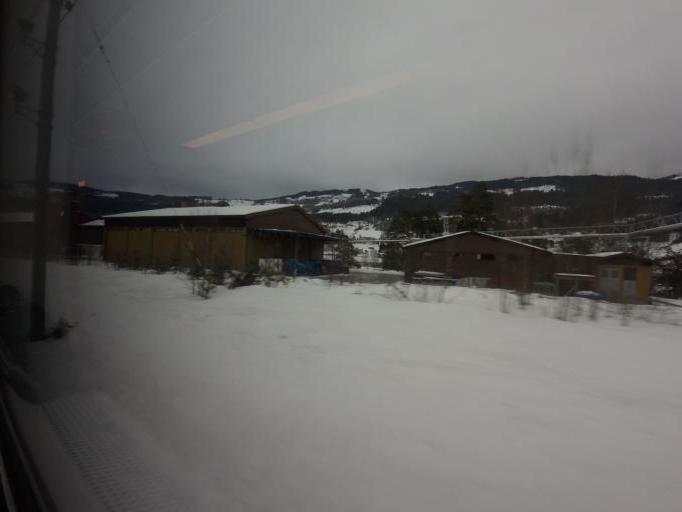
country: NO
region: Oppland
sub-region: Oyer
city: Tretten
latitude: 61.3089
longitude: 10.2967
